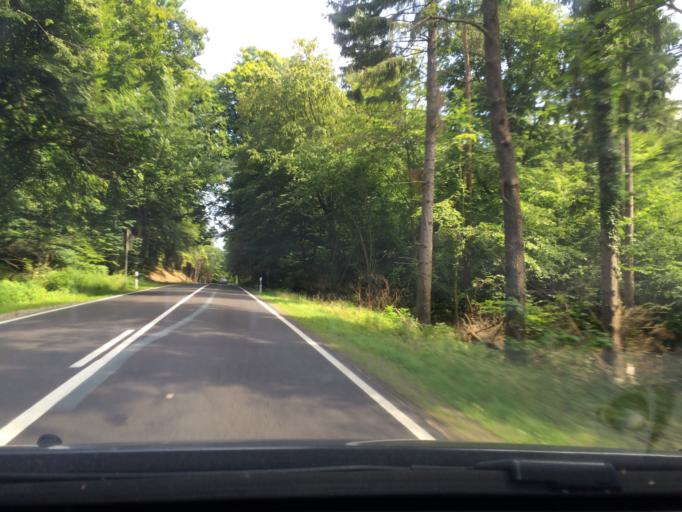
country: DE
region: Mecklenburg-Vorpommern
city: Ostseebad Binz
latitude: 54.4306
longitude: 13.5520
